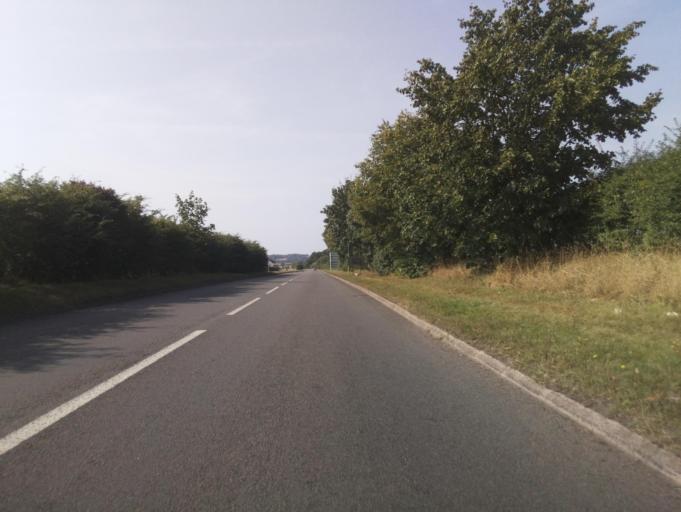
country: GB
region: England
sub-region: Staffordshire
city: Chasetown
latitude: 52.6555
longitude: -1.8835
